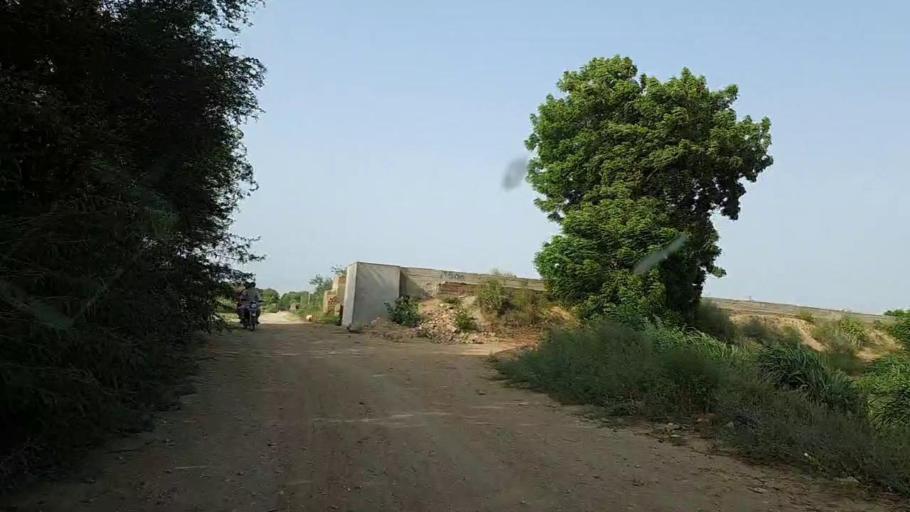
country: PK
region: Sindh
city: Kotri
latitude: 25.2329
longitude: 68.2597
